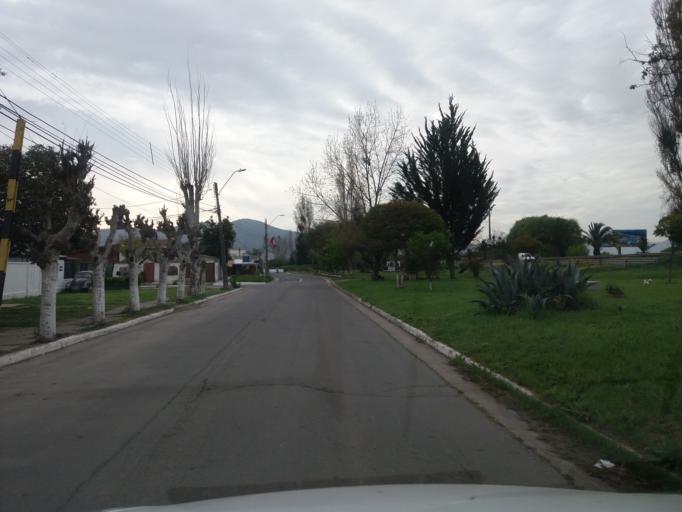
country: CL
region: Valparaiso
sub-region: Provincia de Quillota
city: Hacienda La Calera
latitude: -32.7812
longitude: -71.1775
